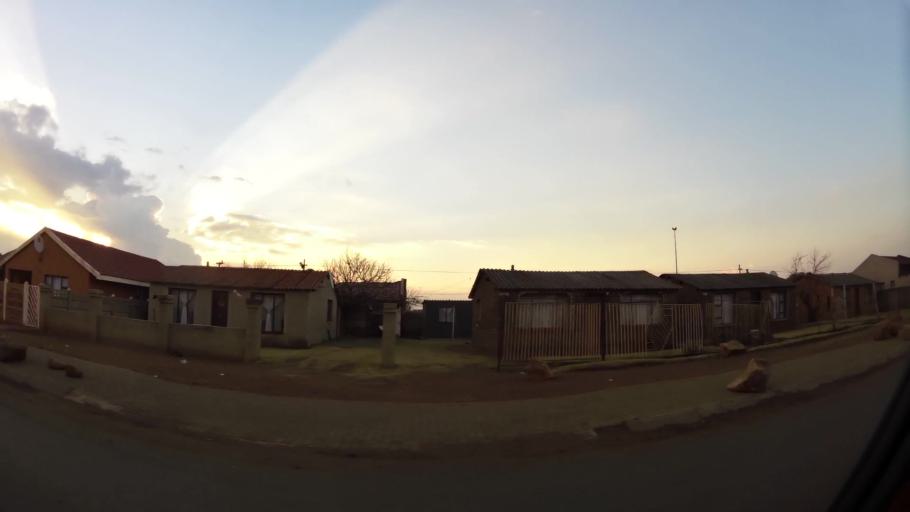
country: ZA
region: Gauteng
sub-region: City of Johannesburg Metropolitan Municipality
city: Orange Farm
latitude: -26.5697
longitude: 27.8453
